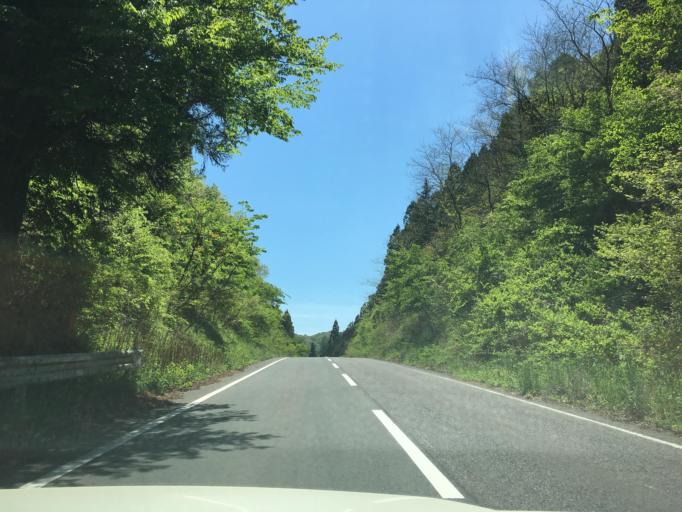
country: JP
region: Fukushima
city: Funehikimachi-funehiki
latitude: 37.3638
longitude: 140.6347
